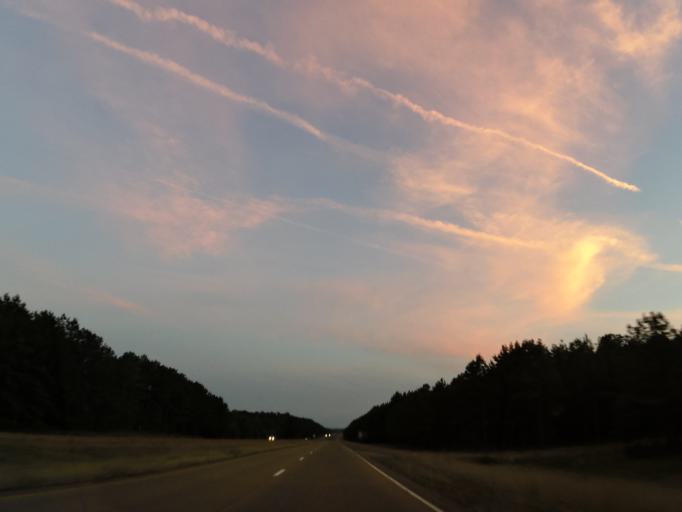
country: US
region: Mississippi
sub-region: Lauderdale County
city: Meridian Station
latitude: 32.5676
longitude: -88.5041
